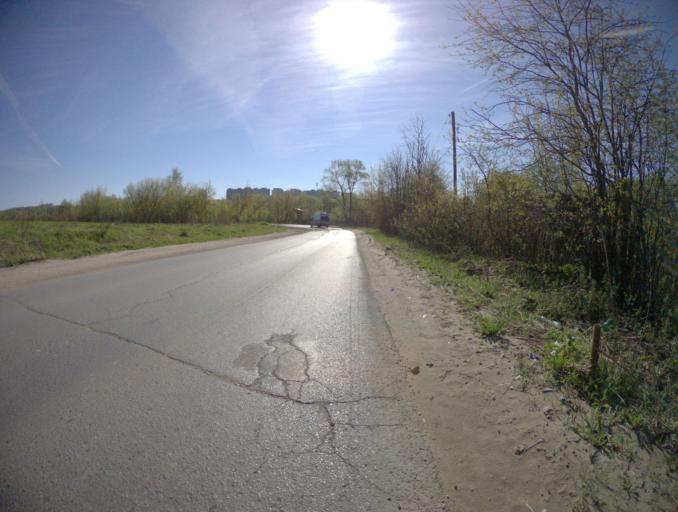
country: RU
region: Vladimir
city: Vladimir
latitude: 56.1614
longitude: 40.3599
